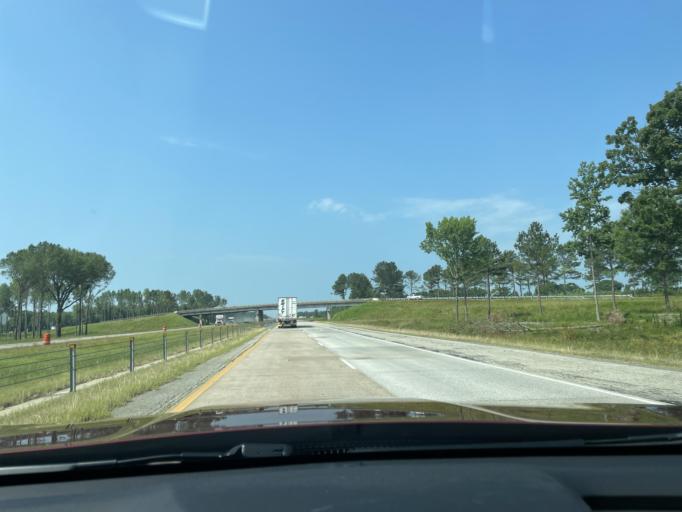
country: US
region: Arkansas
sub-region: White County
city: Searcy
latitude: 35.2053
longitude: -91.7309
